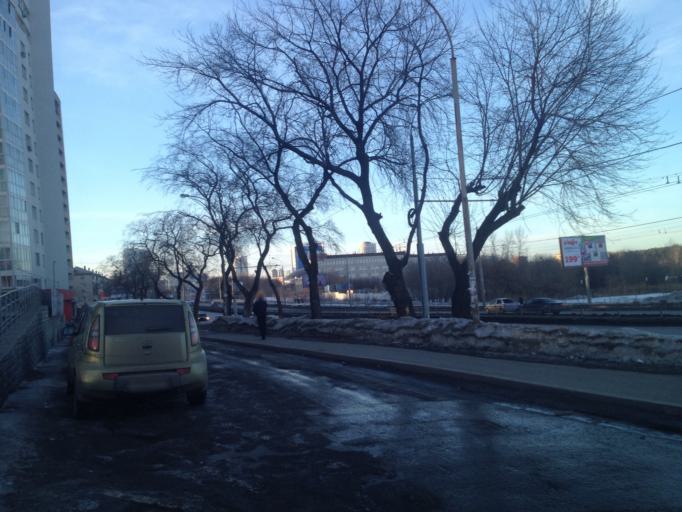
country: RU
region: Sverdlovsk
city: Yekaterinburg
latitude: 56.7840
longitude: 60.6516
